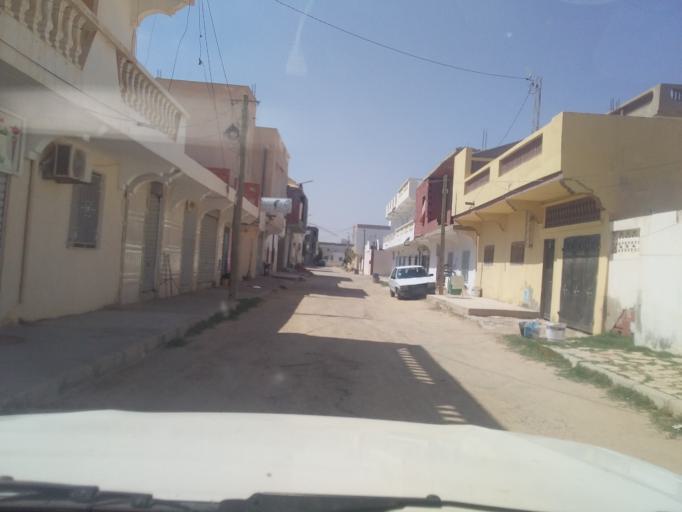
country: TN
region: Qabis
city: Matmata
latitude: 33.6155
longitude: 10.2889
